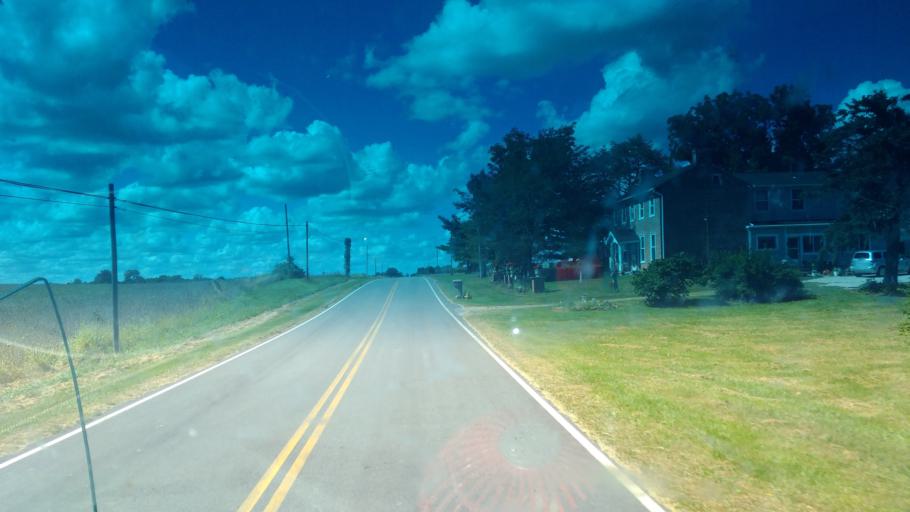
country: US
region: Ohio
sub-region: Union County
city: Marysville
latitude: 40.1841
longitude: -83.4524
